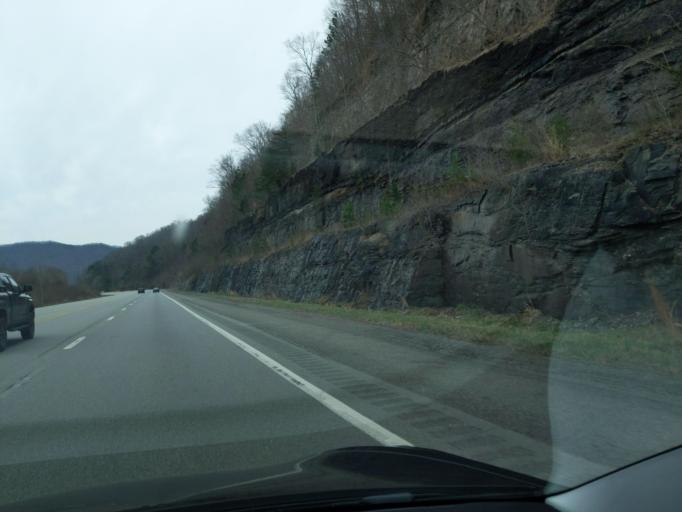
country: US
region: Kentucky
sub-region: Bell County
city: Pineville
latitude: 36.7724
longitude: -83.7303
